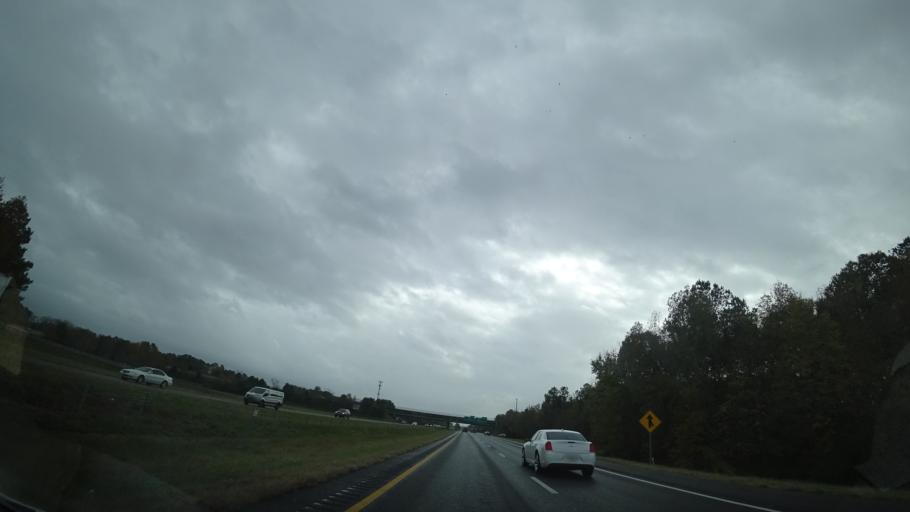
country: US
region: Virginia
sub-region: City of Portsmouth
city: Portsmouth Heights
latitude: 36.8215
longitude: -76.4330
